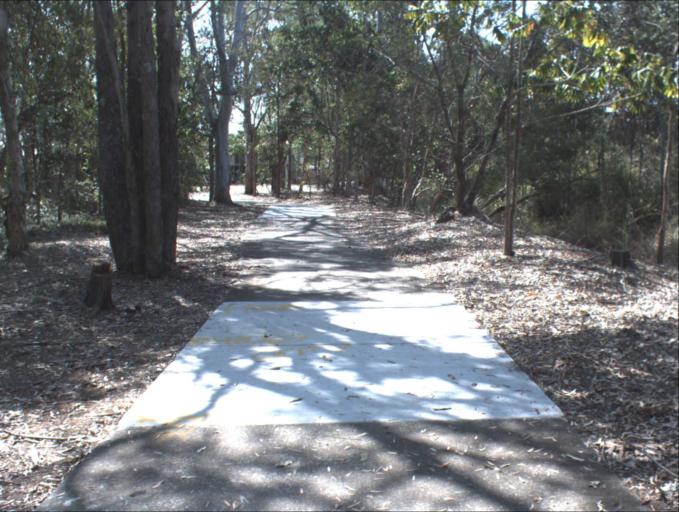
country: AU
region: Queensland
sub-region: Logan
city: Beenleigh
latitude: -27.6888
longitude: 153.1895
